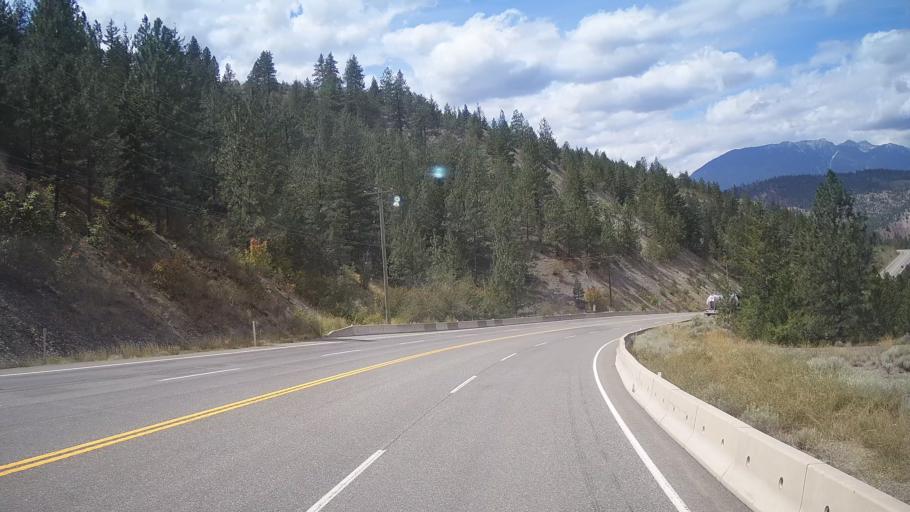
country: CA
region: British Columbia
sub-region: Thompson-Nicola Regional District
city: Ashcroft
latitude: 50.2544
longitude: -121.5162
